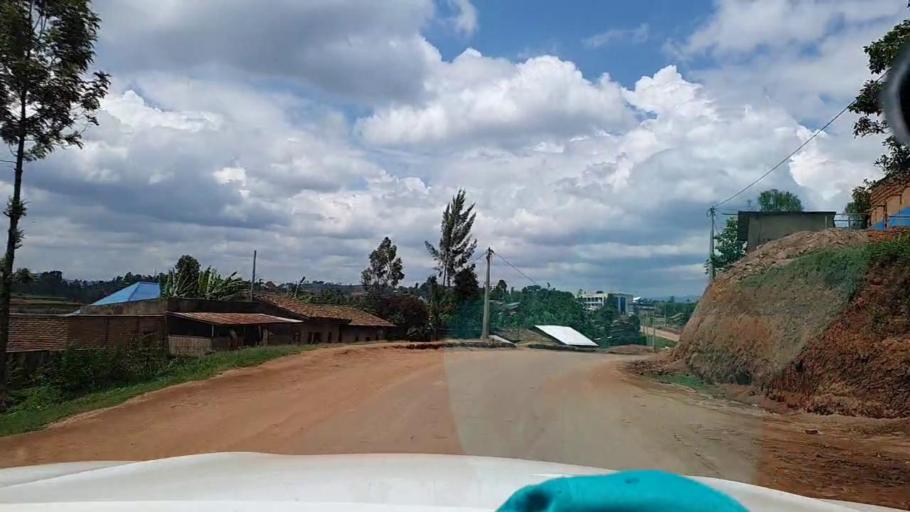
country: RW
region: Southern Province
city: Nzega
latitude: -2.6474
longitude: 29.5643
